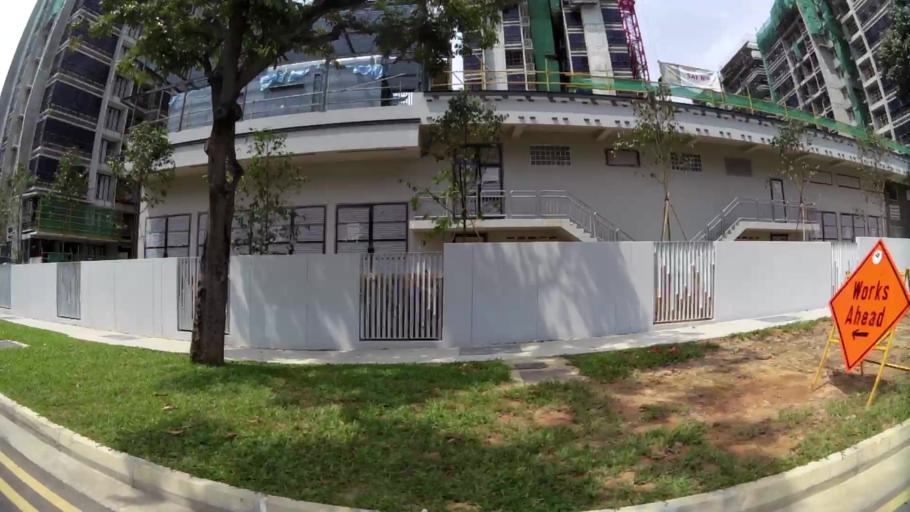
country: MY
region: Johor
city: Kampung Pasir Gudang Baru
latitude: 1.3713
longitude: 103.9470
